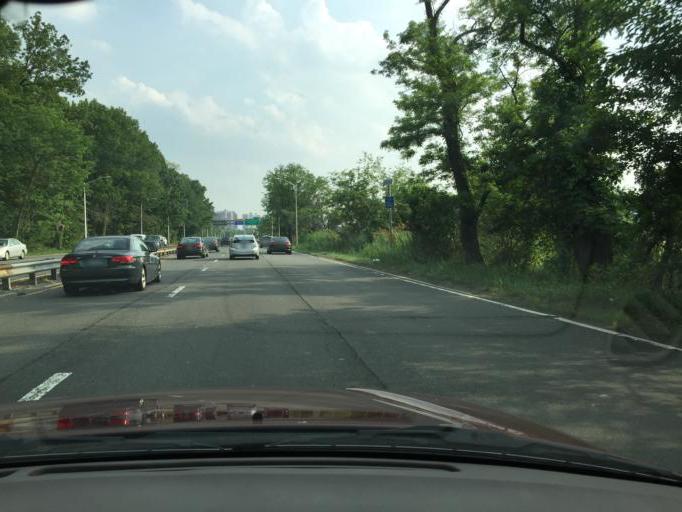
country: US
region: New York
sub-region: Westchester County
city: Pelham Manor
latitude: 40.8814
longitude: -73.8169
